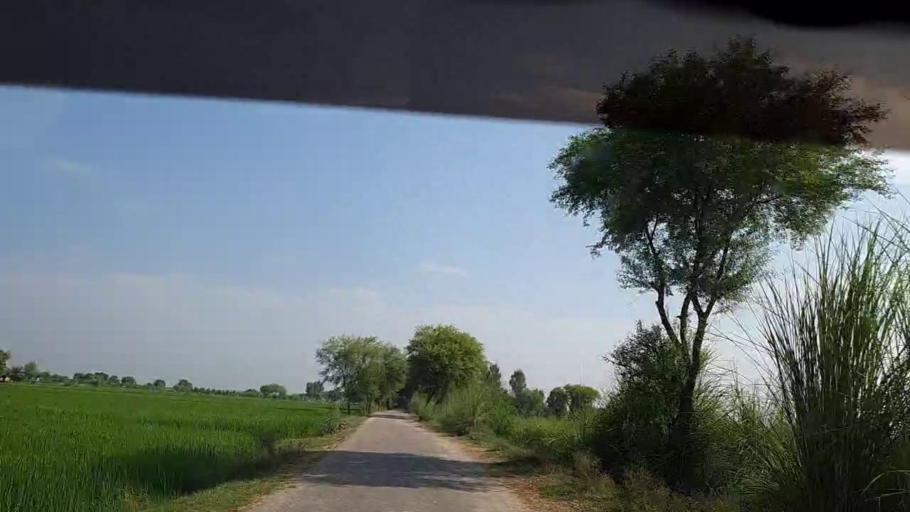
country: PK
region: Sindh
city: Shikarpur
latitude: 28.0953
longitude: 68.6754
